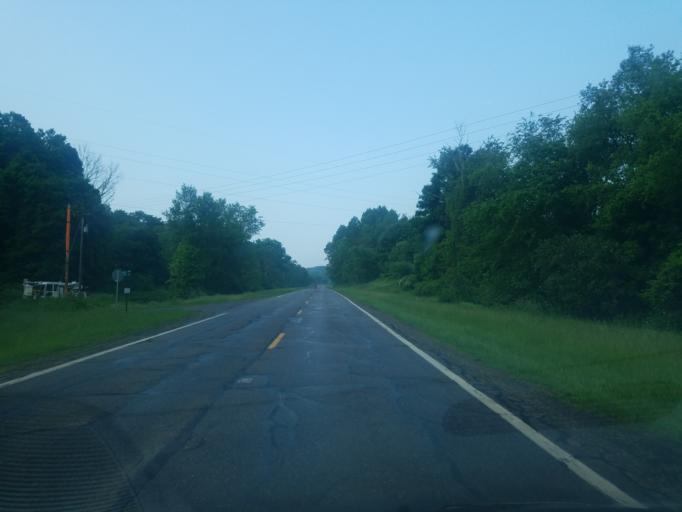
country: US
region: Ohio
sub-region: Tuscarawas County
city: Rockford
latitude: 40.5222
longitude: -81.2572
